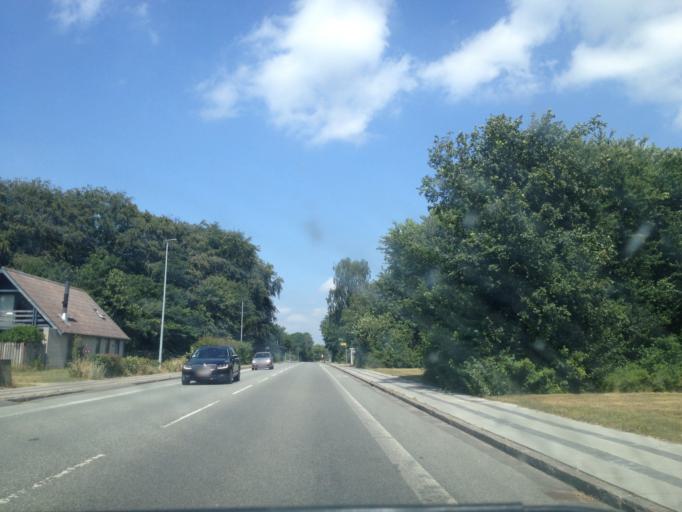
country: DK
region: South Denmark
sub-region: Kolding Kommune
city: Vamdrup
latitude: 55.4337
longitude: 9.2907
